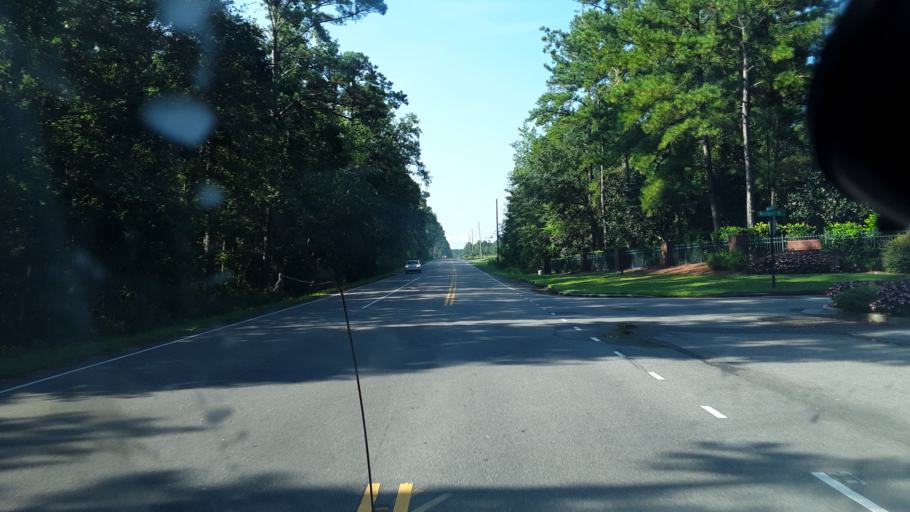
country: US
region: North Carolina
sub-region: Brunswick County
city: Belville
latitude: 34.1915
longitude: -77.9867
